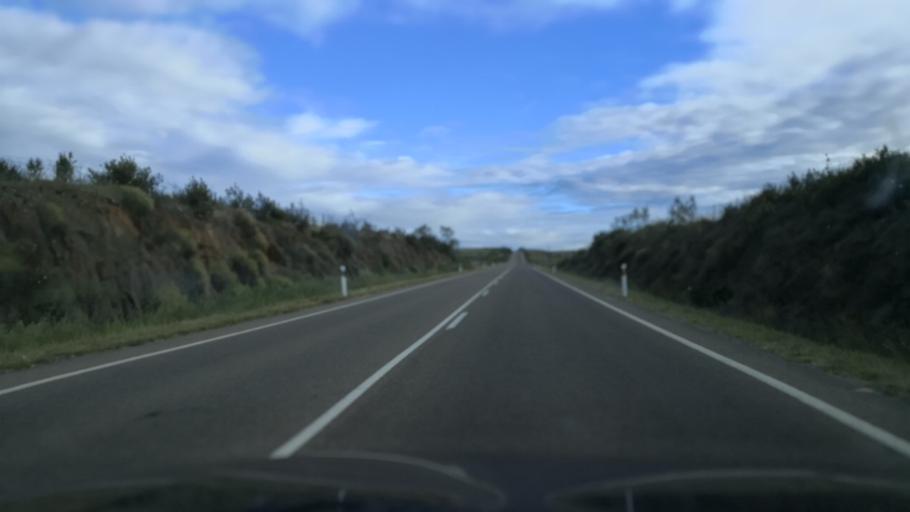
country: ES
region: Extremadura
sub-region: Provincia de Caceres
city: Coria
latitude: 39.9419
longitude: -6.5072
